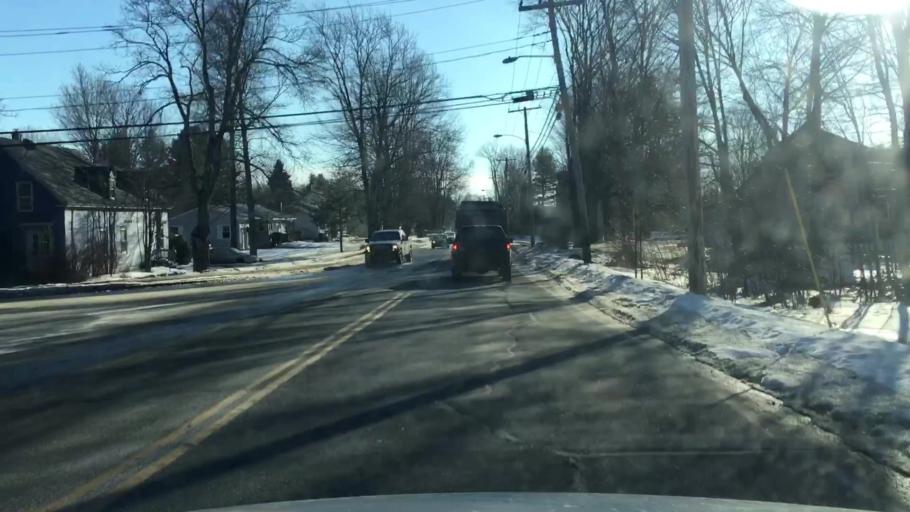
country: US
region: Maine
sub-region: Cumberland County
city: Westbrook
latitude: 43.6953
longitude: -70.3577
